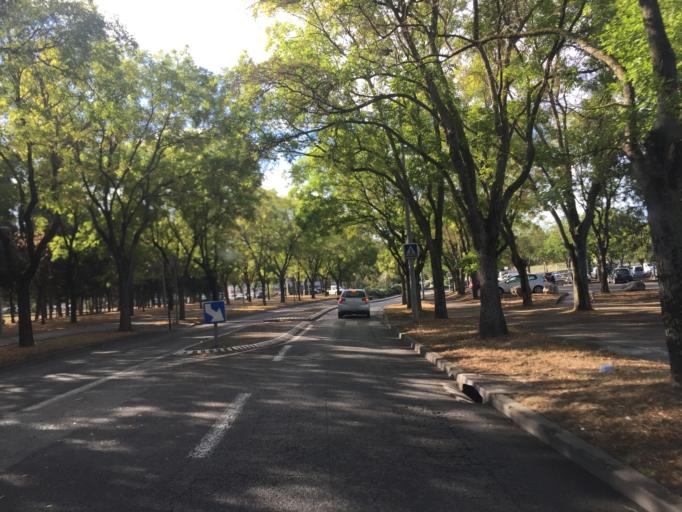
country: FR
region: Provence-Alpes-Cote d'Azur
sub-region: Departement des Bouches-du-Rhone
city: Aix-en-Provence
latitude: 43.5274
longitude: 5.4239
